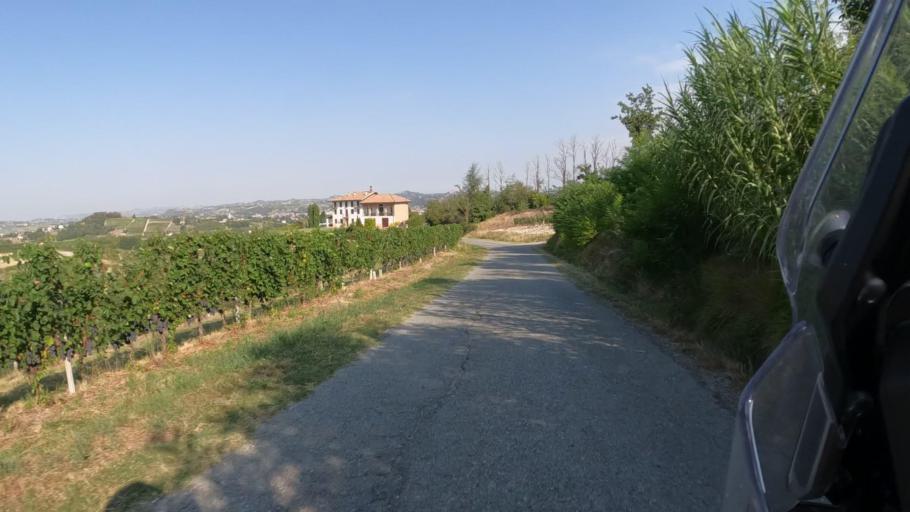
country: IT
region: Piedmont
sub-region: Provincia di Asti
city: Nizza Monferrato
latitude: 44.7575
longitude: 8.3820
